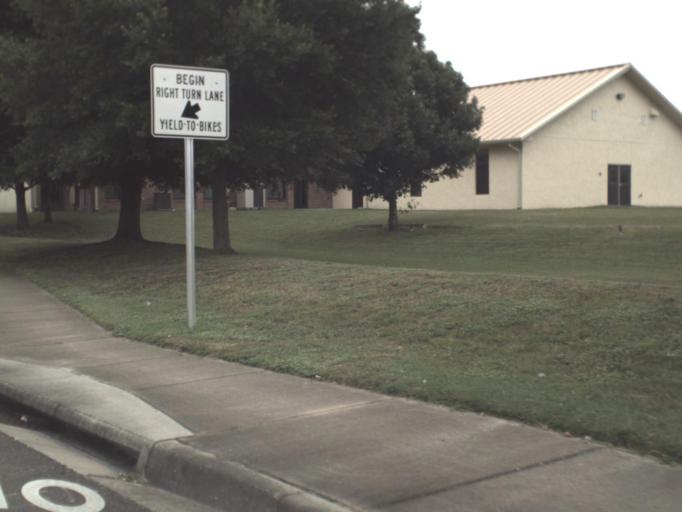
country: US
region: Florida
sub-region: Pasco County
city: Elfers
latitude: 28.2169
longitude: -82.7201
